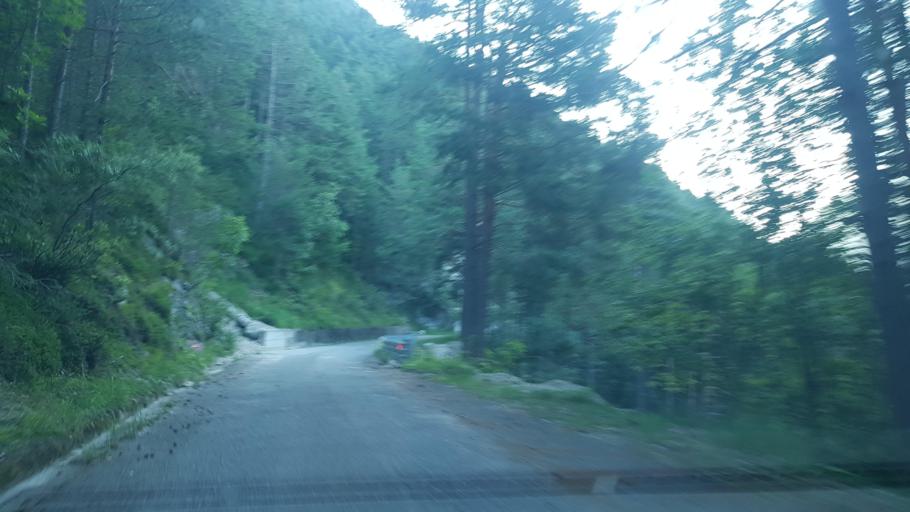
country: IT
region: Friuli Venezia Giulia
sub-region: Provincia di Udine
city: Malborghetto
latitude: 46.4555
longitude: 13.3936
